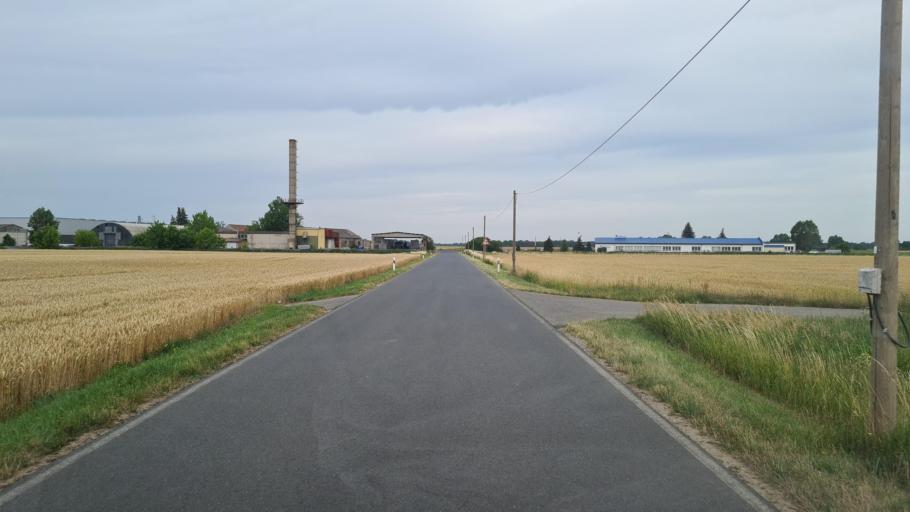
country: DE
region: Saxony-Anhalt
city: Jessen
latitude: 51.7559
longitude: 12.9563
